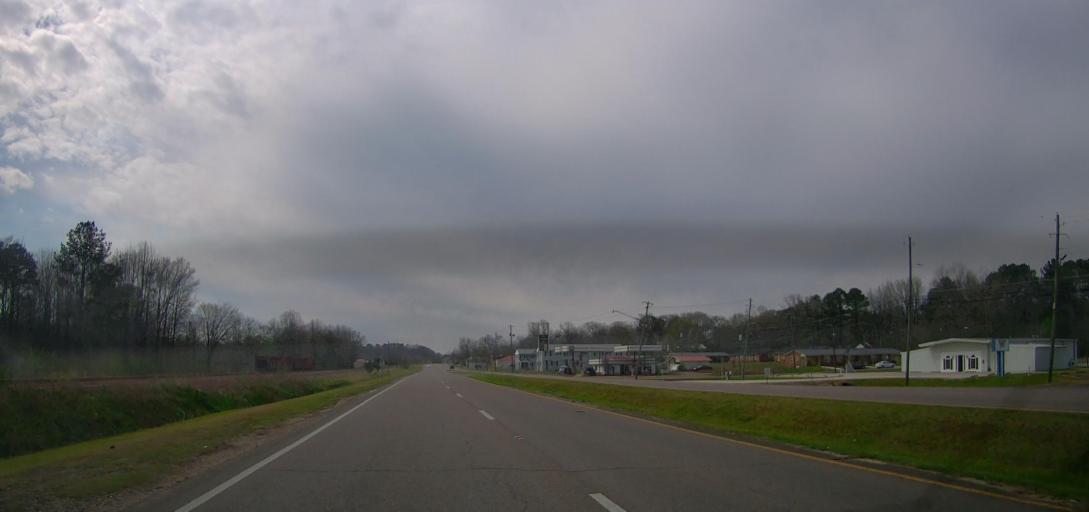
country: US
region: Alabama
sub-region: Walker County
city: Carbon Hill
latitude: 33.8859
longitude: -87.5216
